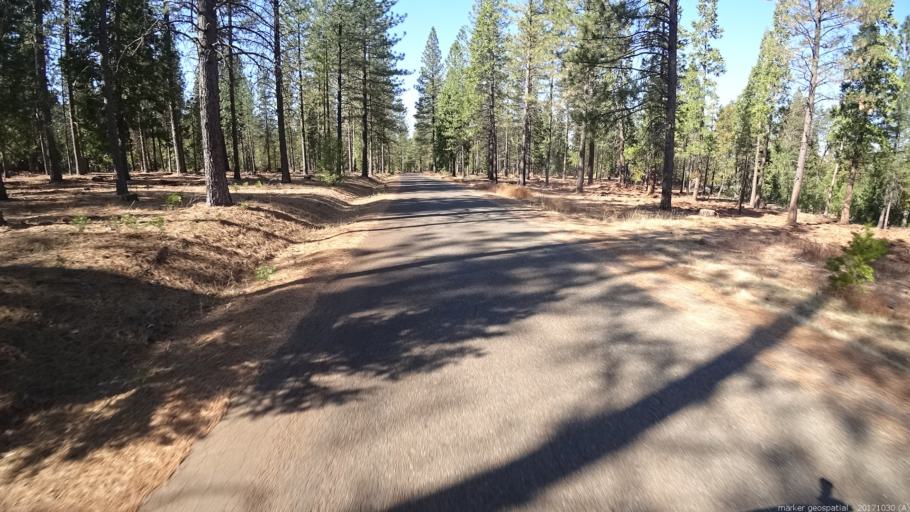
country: US
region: California
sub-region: Shasta County
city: Shingletown
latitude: 40.6188
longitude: -121.8906
